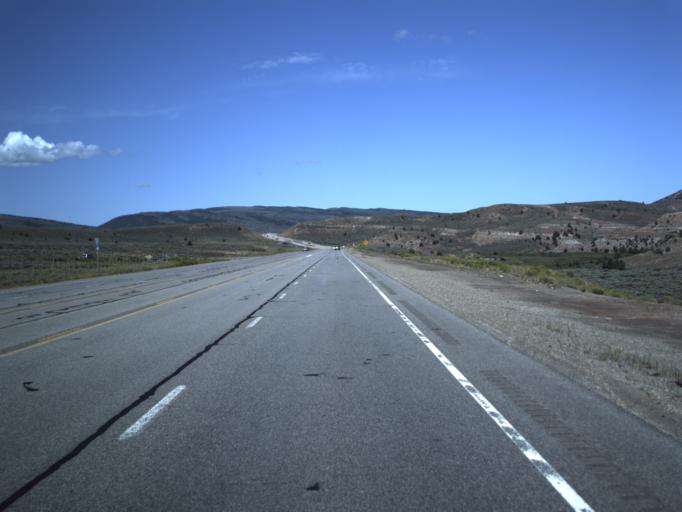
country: US
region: Utah
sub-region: Carbon County
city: Helper
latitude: 39.8385
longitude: -110.9829
